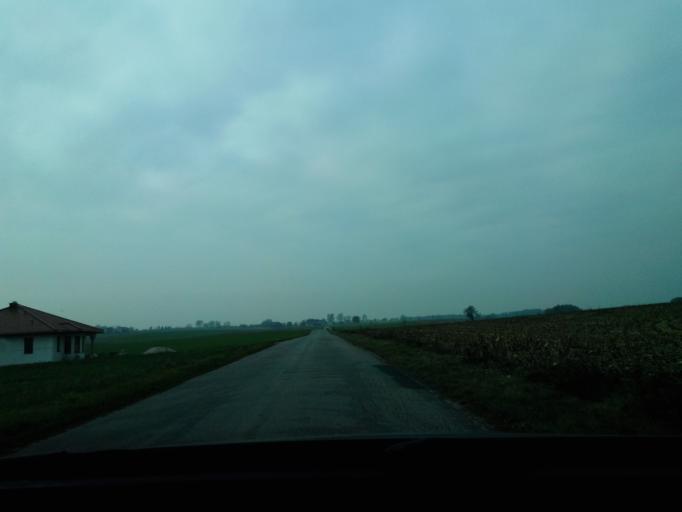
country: PL
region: Kujawsko-Pomorskie
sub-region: Powiat brodnicki
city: Swiedziebnia
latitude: 53.2089
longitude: 19.5398
